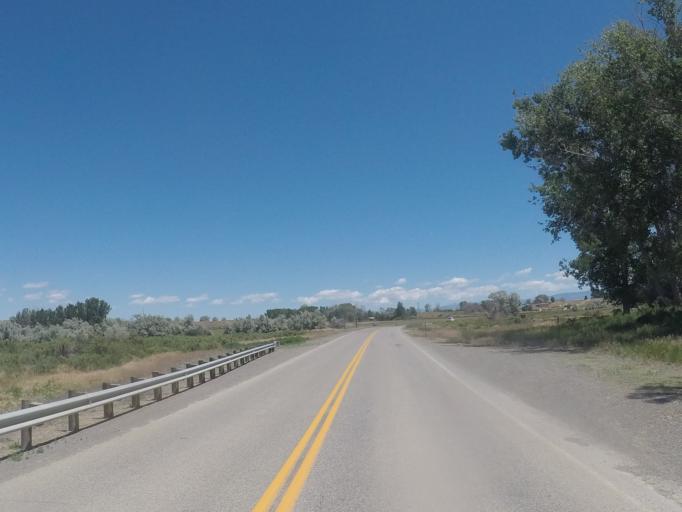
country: US
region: Wyoming
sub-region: Big Horn County
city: Lovell
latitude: 44.7992
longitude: -108.4318
